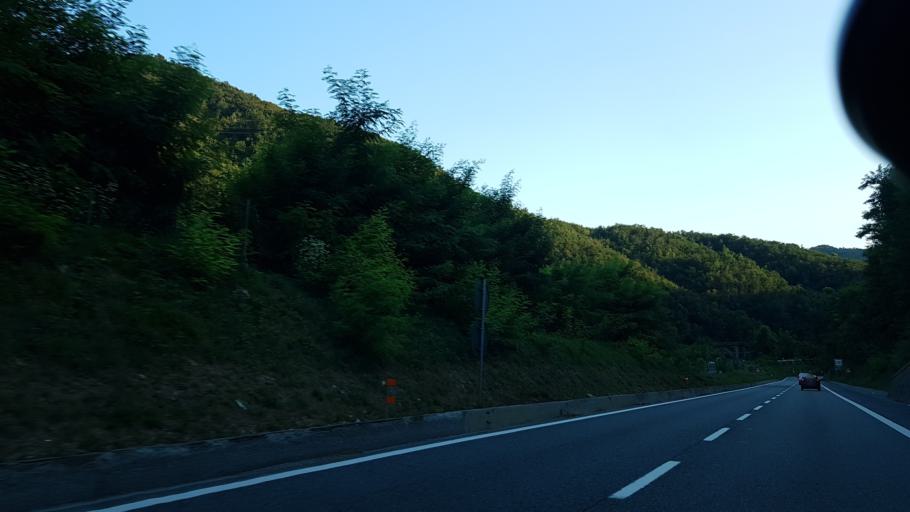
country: IT
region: Liguria
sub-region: Provincia di Genova
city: Isola del Cantone
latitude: 44.6379
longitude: 8.9513
